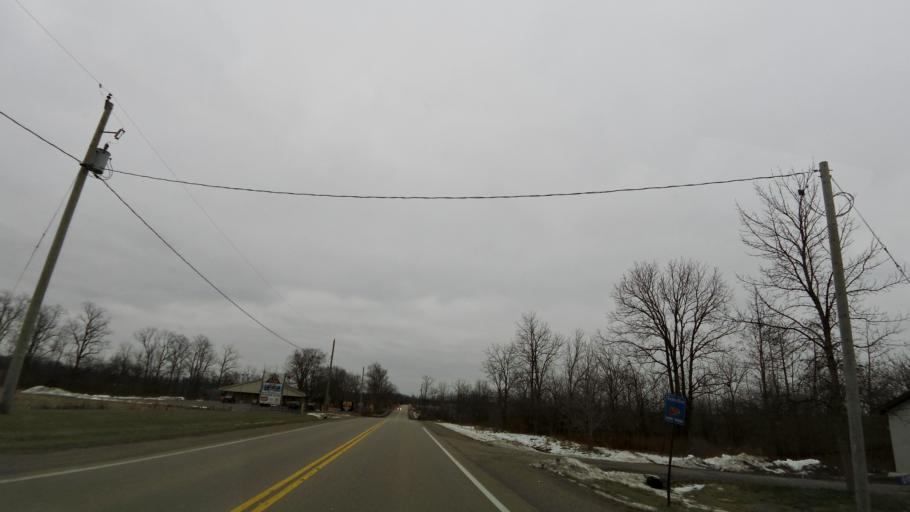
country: CA
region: Ontario
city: Ancaster
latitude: 43.1111
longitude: -80.1068
